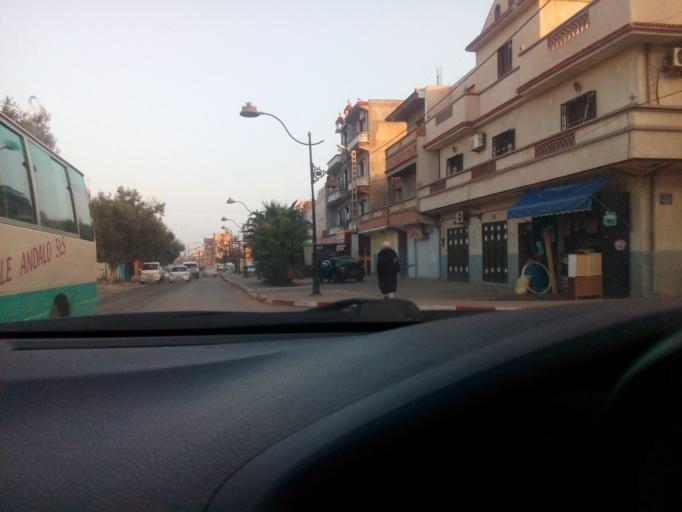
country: DZ
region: Oran
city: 'Ain el Turk
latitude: 35.7376
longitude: -0.7724
